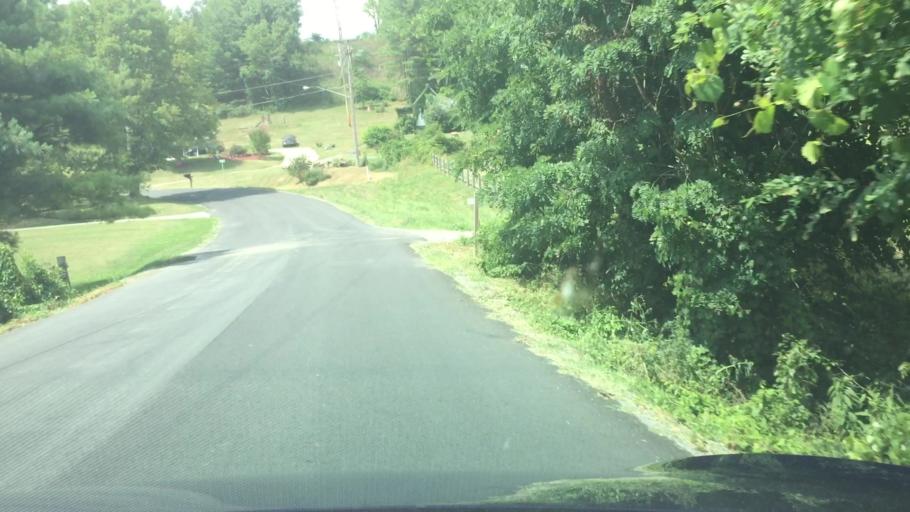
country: US
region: Virginia
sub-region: Wythe County
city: Wytheville
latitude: 36.9379
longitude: -81.0739
